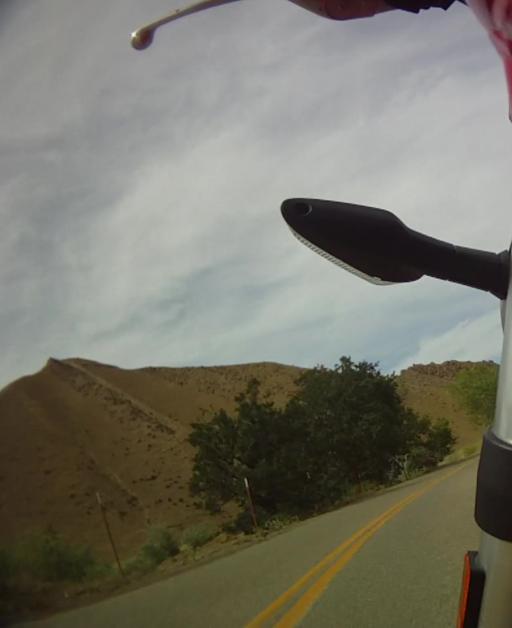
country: US
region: California
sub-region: Stanislaus County
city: Patterson
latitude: 37.4589
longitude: -121.2555
